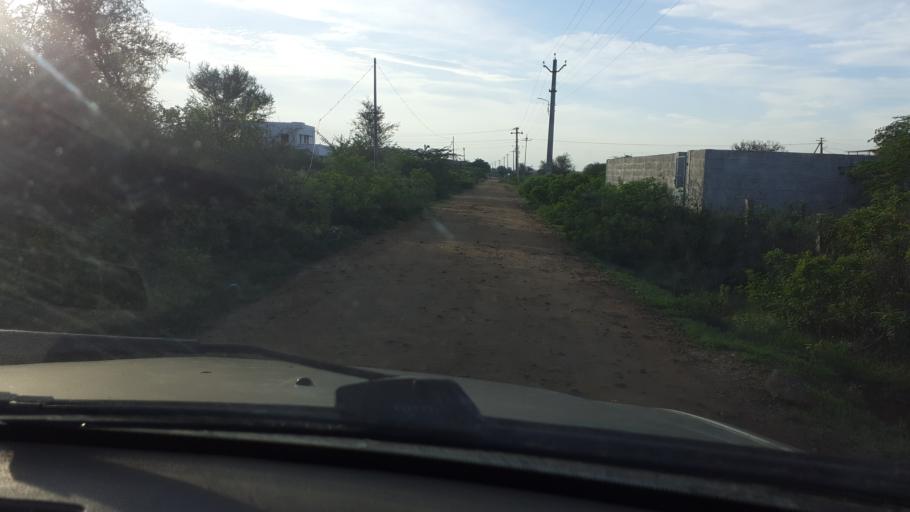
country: IN
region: Tamil Nadu
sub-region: Tirunelveli Kattabo
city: Tirunelveli
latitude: 8.6716
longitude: 77.7179
